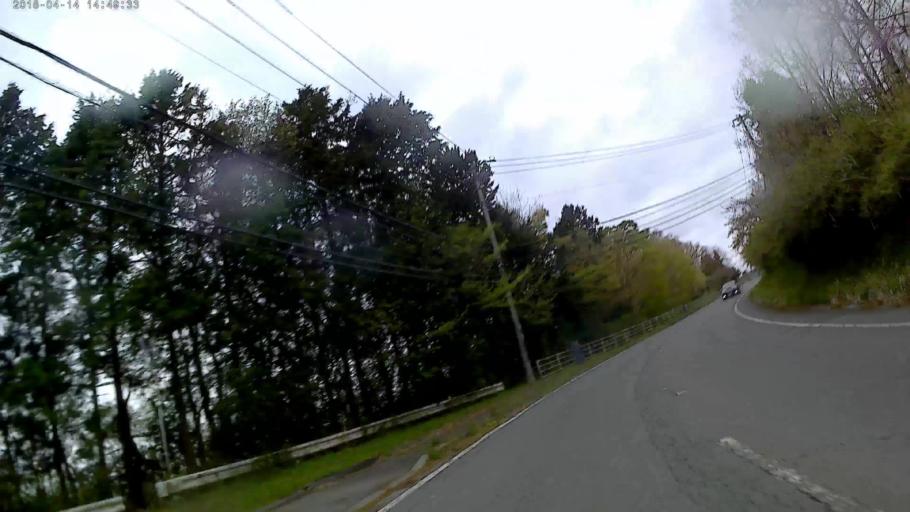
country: JP
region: Shizuoka
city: Gotemba
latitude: 35.3614
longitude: 138.9738
